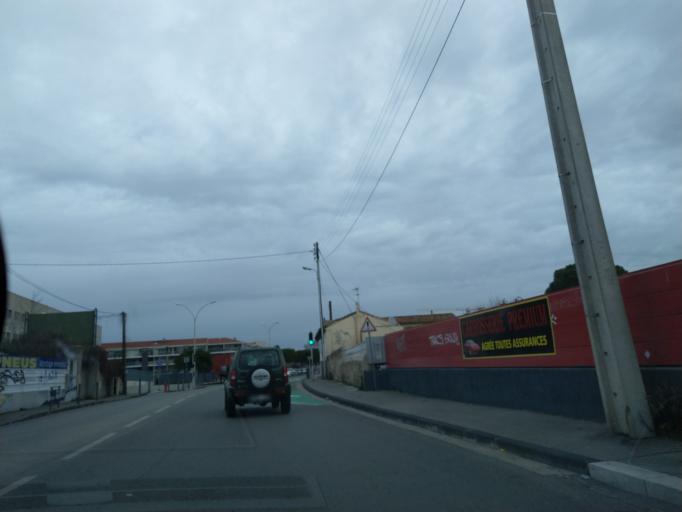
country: FR
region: Provence-Alpes-Cote d'Azur
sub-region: Departement des Bouches-du-Rhone
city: Marseille 12
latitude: 43.2954
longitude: 5.4333
